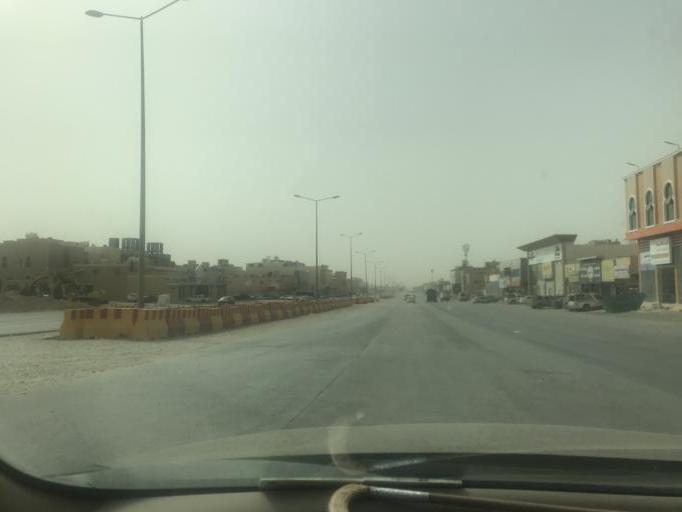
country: SA
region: Ar Riyad
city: Riyadh
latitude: 24.8102
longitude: 46.6005
